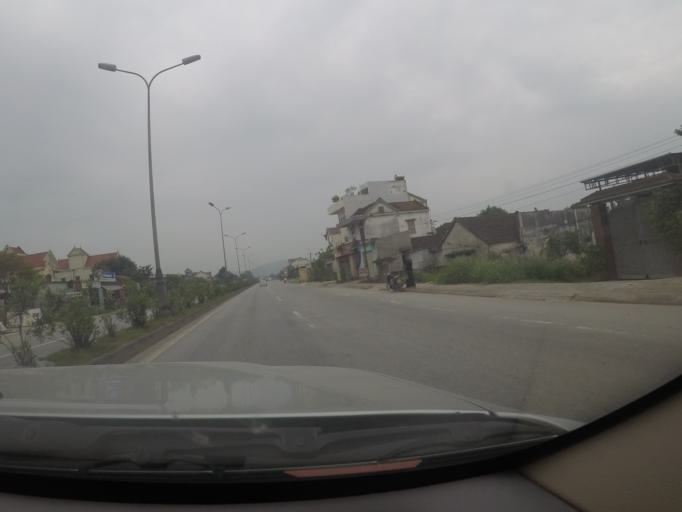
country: VN
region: Nghe An
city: Dien Chau
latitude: 18.9407
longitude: 105.6047
